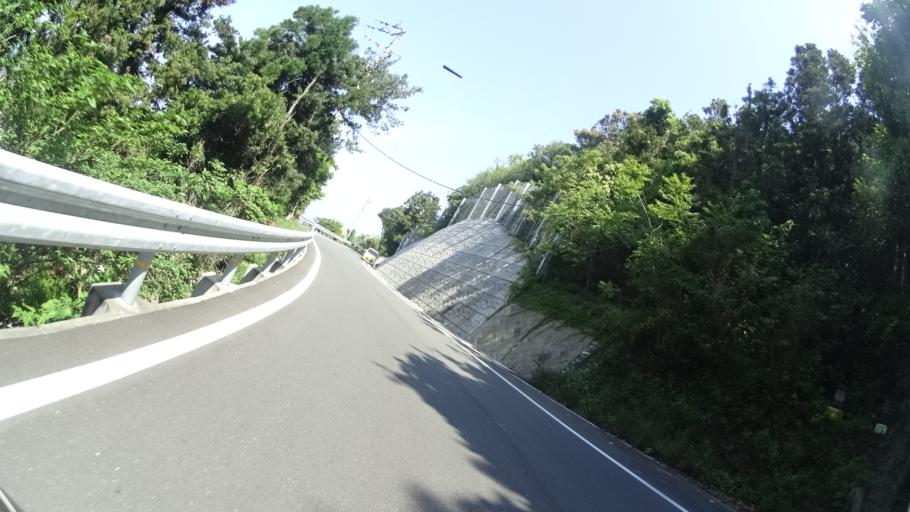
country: JP
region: Oita
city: Tsukumiura
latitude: 33.3550
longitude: 132.0322
